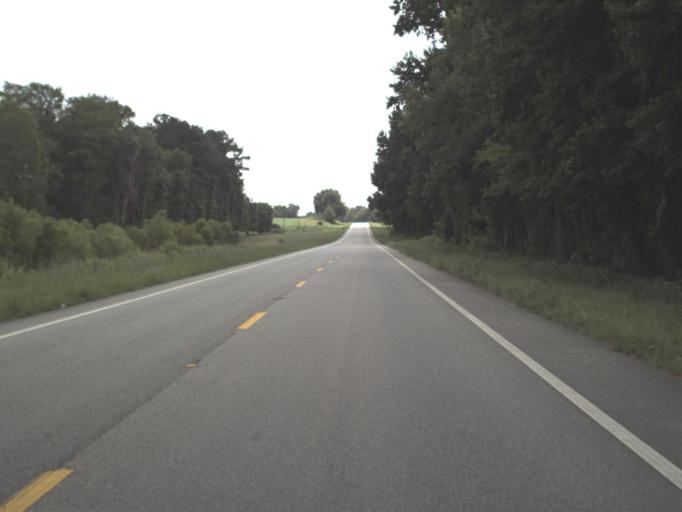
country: US
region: Florida
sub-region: Madison County
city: Madison
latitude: 30.4701
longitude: -83.5926
